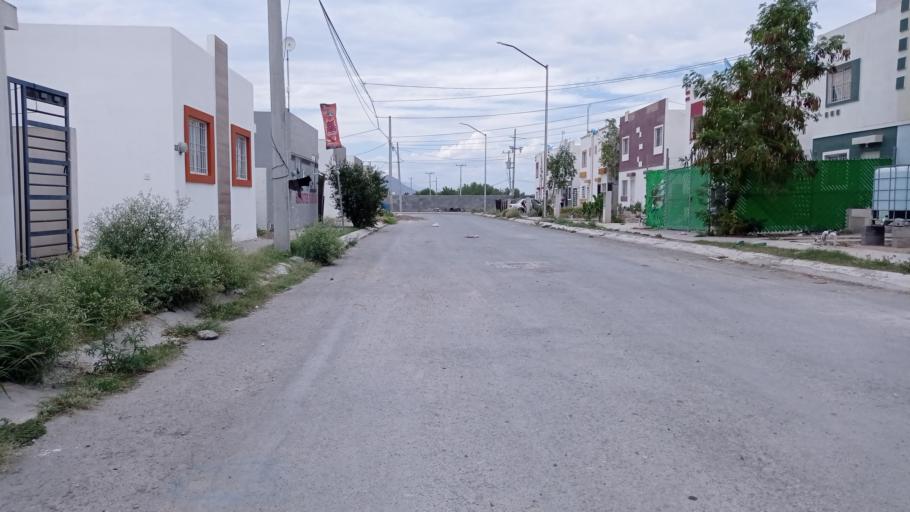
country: MX
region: Nuevo Leon
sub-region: Salinas Victoria
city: Simeprodeso (Colectivo Nuevo)
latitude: 25.8753
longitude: -100.3144
